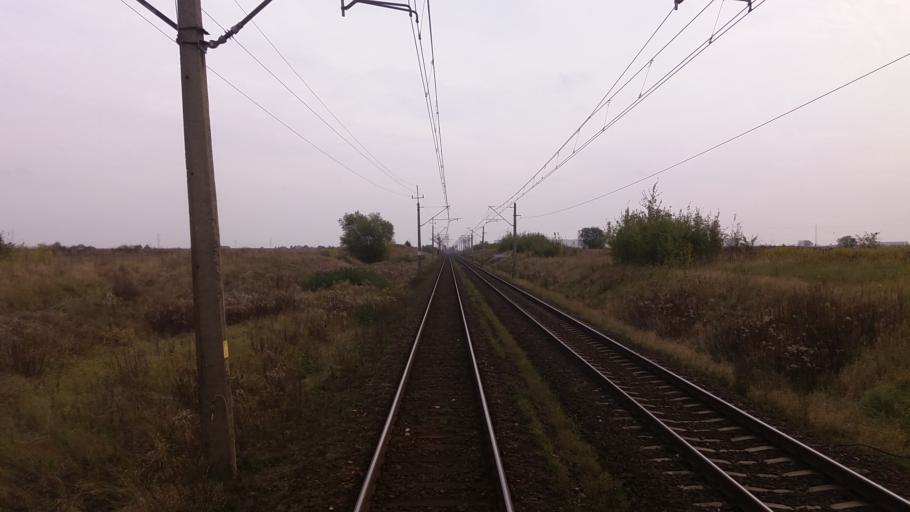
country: PL
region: West Pomeranian Voivodeship
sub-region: Powiat stargardzki
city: Stargard Szczecinski
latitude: 53.3565
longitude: 14.9859
